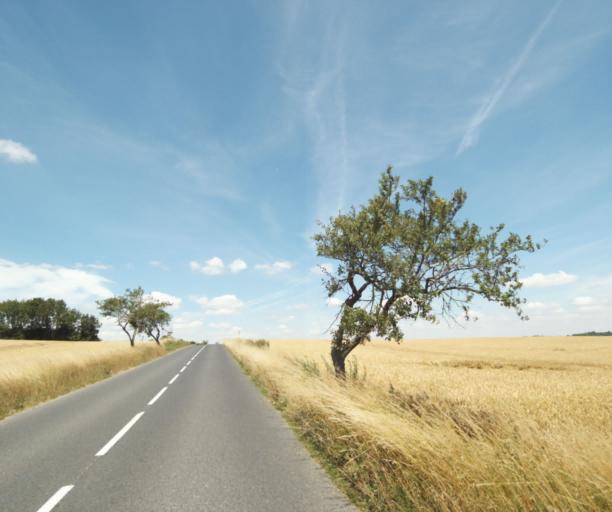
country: FR
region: Lorraine
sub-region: Departement de Meurthe-et-Moselle
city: Luneville
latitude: 48.6144
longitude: 6.4719
